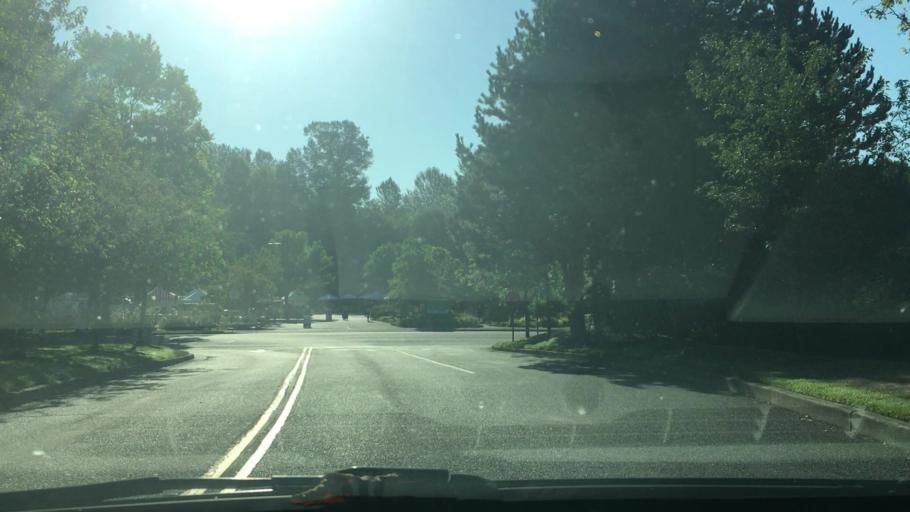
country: US
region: Washington
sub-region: King County
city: Issaquah
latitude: 47.5507
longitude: -122.0505
